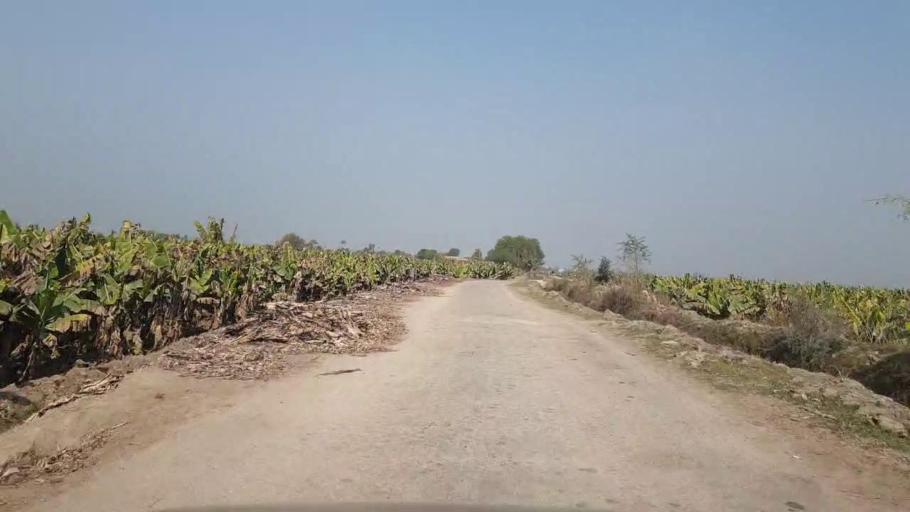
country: PK
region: Sindh
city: Bhit Shah
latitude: 25.7859
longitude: 68.4932
